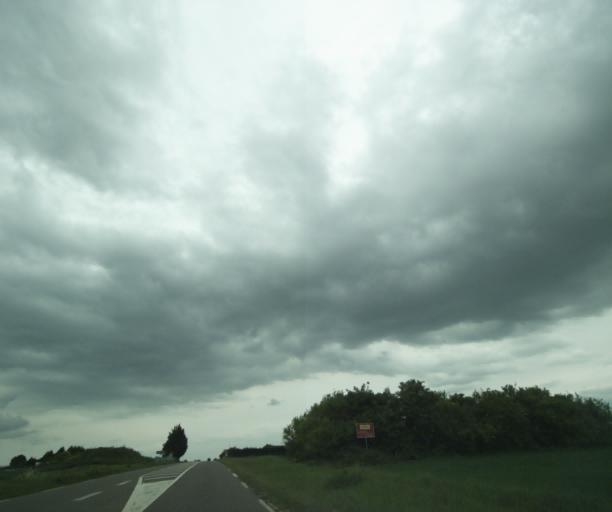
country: FR
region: Ile-de-France
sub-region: Departement des Yvelines
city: Bouafle
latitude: 48.9569
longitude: 1.8930
